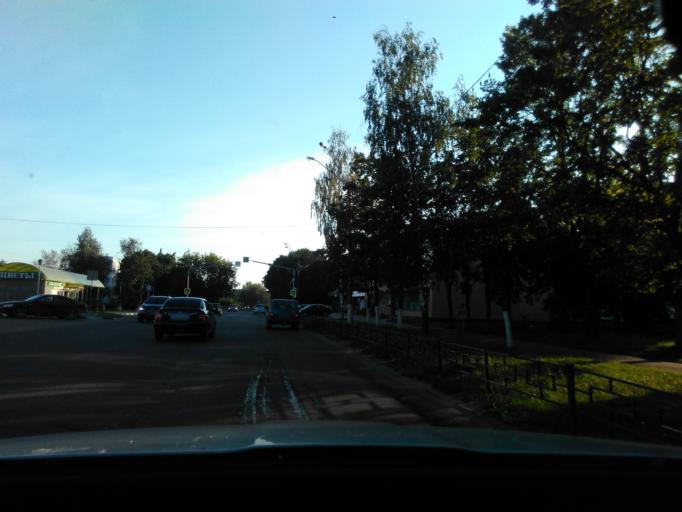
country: RU
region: Tverskaya
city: Konakovo
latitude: 56.7117
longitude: 36.7765
